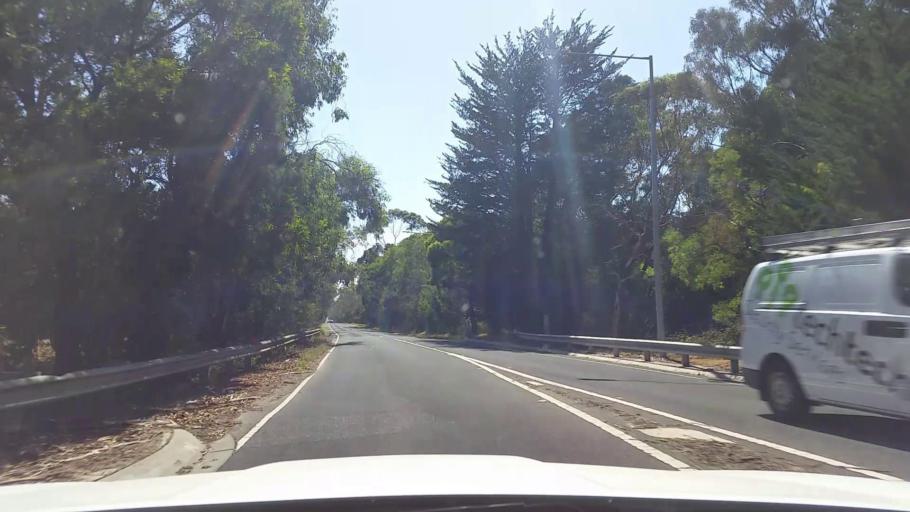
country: AU
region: Victoria
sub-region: Mornington Peninsula
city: Somerville
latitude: -38.2348
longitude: 145.1514
